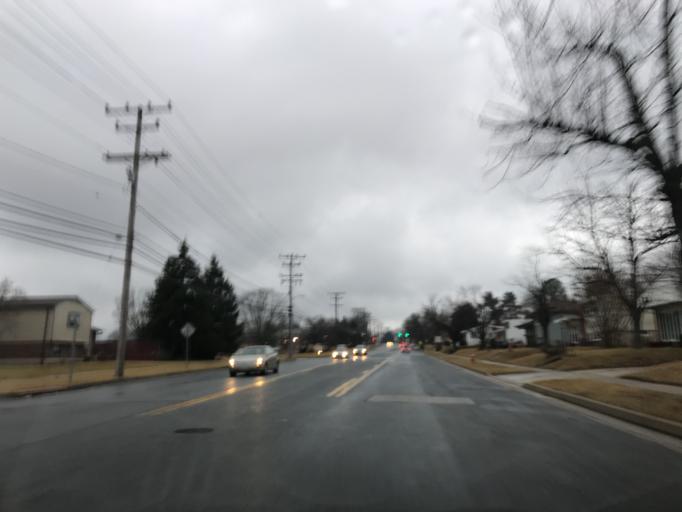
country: US
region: Maryland
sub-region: Baltimore County
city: Pikesville
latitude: 39.3760
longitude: -76.6891
